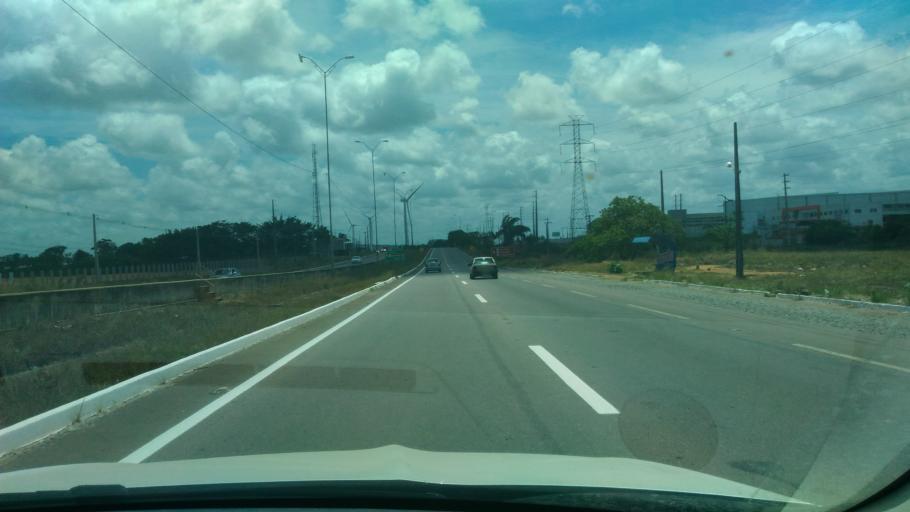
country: BR
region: Paraiba
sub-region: Conde
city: Conde
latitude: -7.2534
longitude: -34.9337
